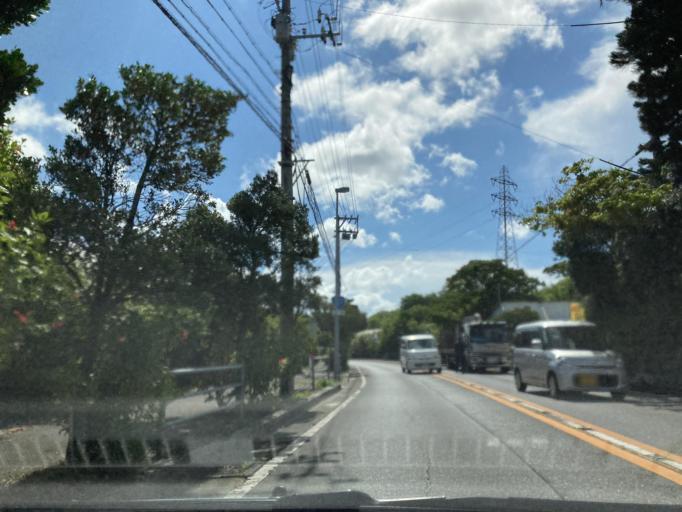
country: JP
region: Okinawa
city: Tomigusuku
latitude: 26.1662
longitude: 127.7207
